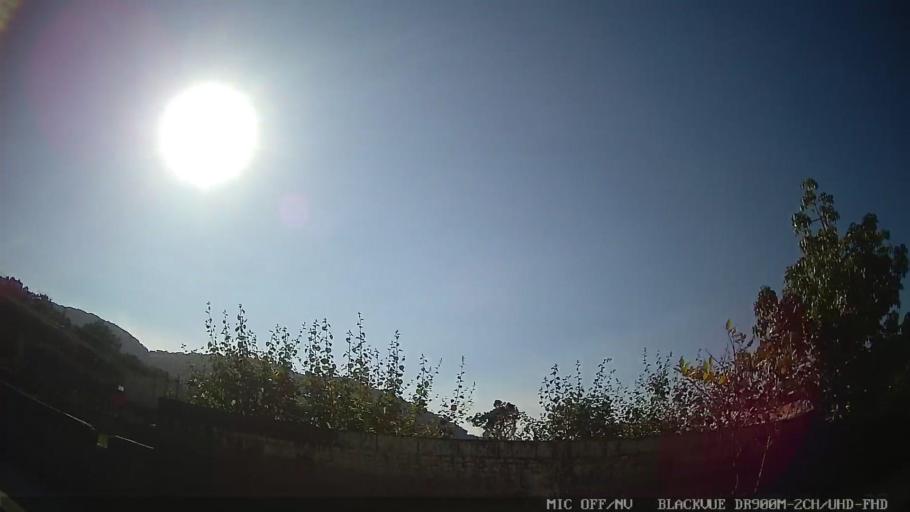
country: BR
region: Sao Paulo
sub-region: Guaruja
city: Guaruja
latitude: -23.9689
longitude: -46.2132
